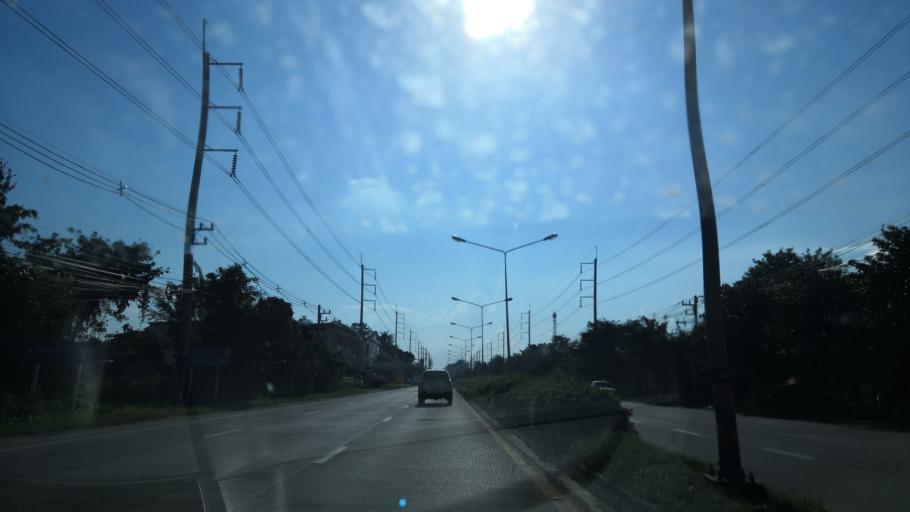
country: TH
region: Chiang Mai
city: San Sai
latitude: 18.8505
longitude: 99.0865
